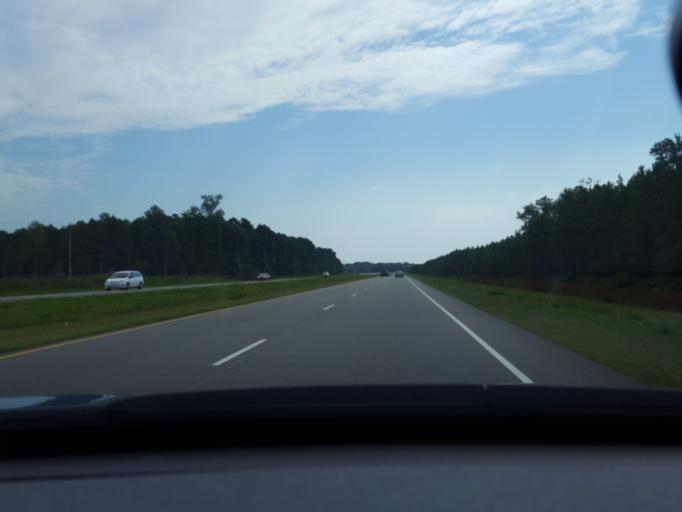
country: US
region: North Carolina
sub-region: Chowan County
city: Edenton
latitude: 36.0372
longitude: -76.7328
